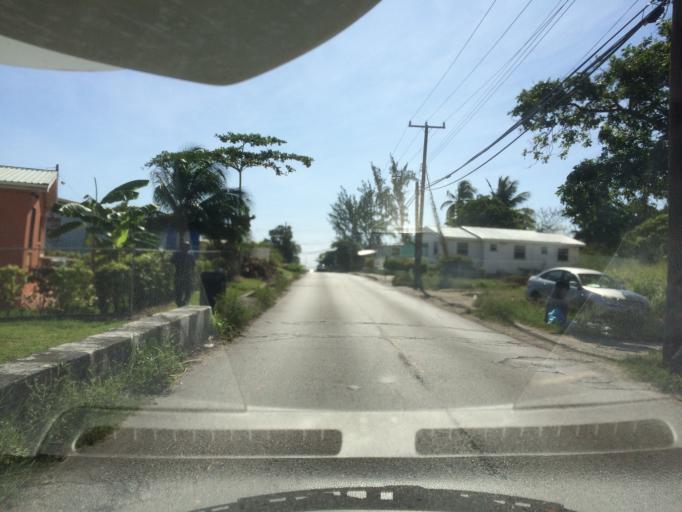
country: BB
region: Christ Church
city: Oistins
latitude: 13.0722
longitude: -59.5394
